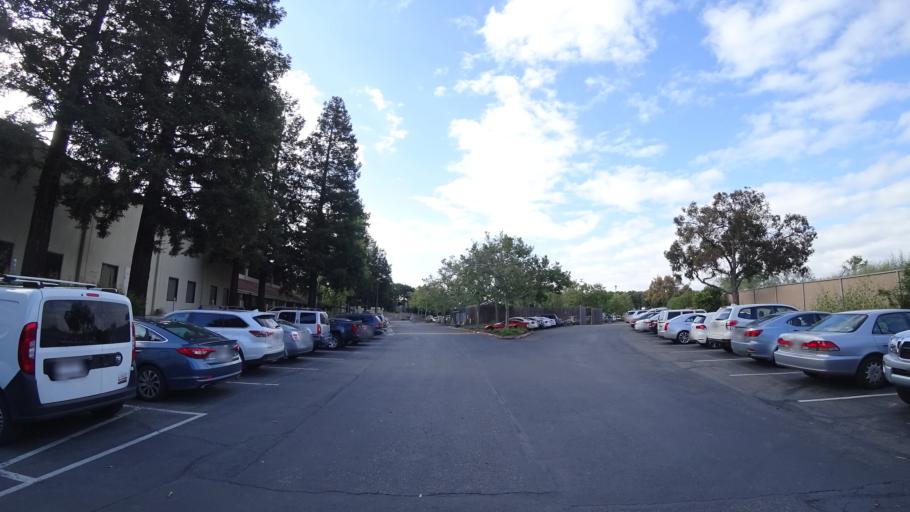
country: US
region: California
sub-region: Santa Clara County
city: Milpitas
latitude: 37.3998
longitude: -121.9408
